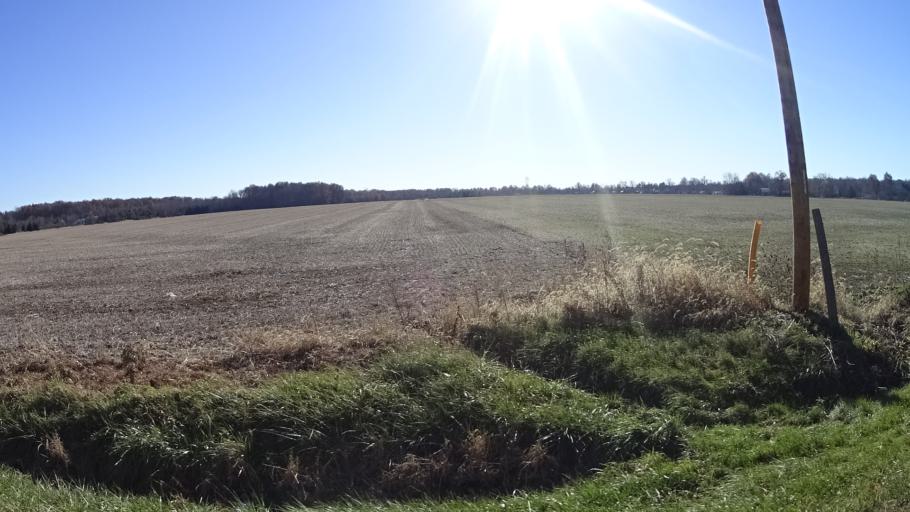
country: US
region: Ohio
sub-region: Lorain County
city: Grafton
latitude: 41.2748
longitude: -82.0957
